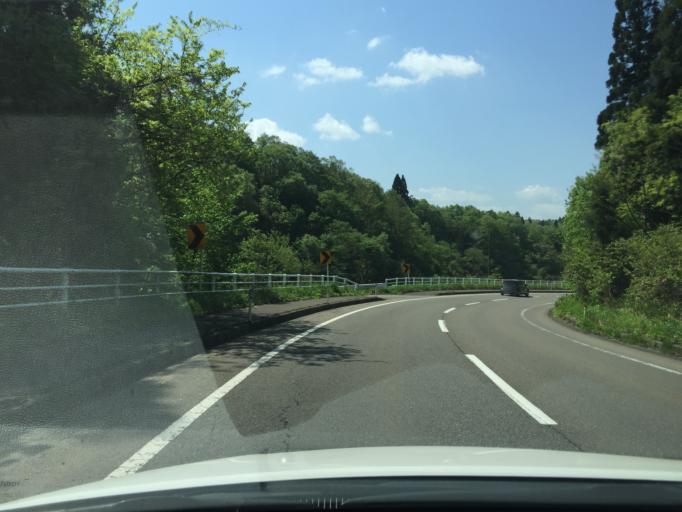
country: JP
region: Niigata
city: Kamo
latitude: 37.5812
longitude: 139.0939
